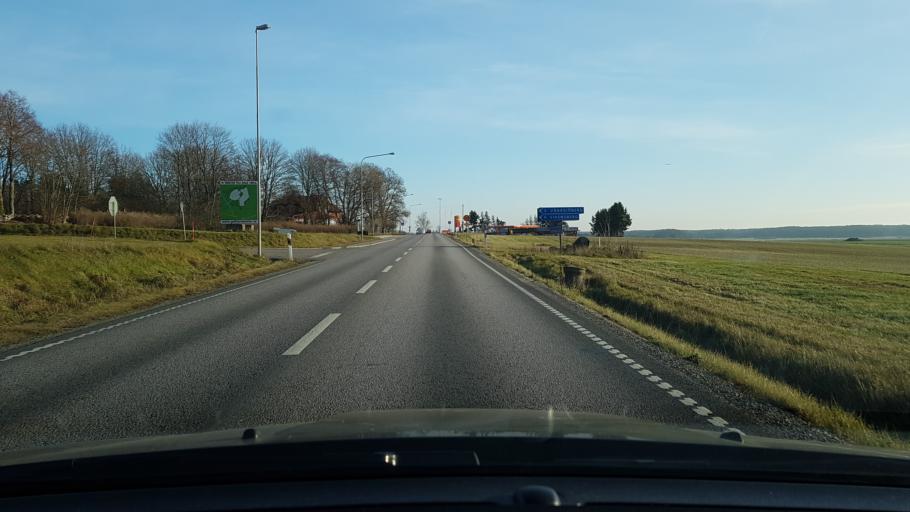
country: SE
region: Stockholm
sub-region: Norrtalje Kommun
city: Nykvarn
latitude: 59.7397
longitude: 18.1564
